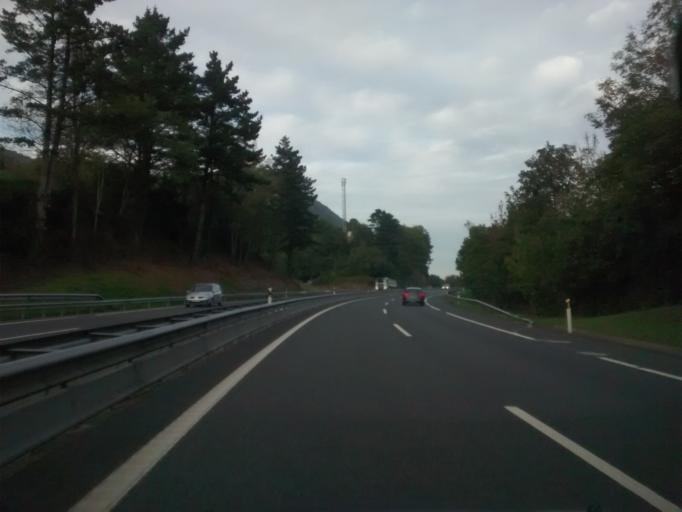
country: ES
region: Basque Country
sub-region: Provincia de Guipuzcoa
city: Mendaro
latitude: 43.2495
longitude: -2.3933
